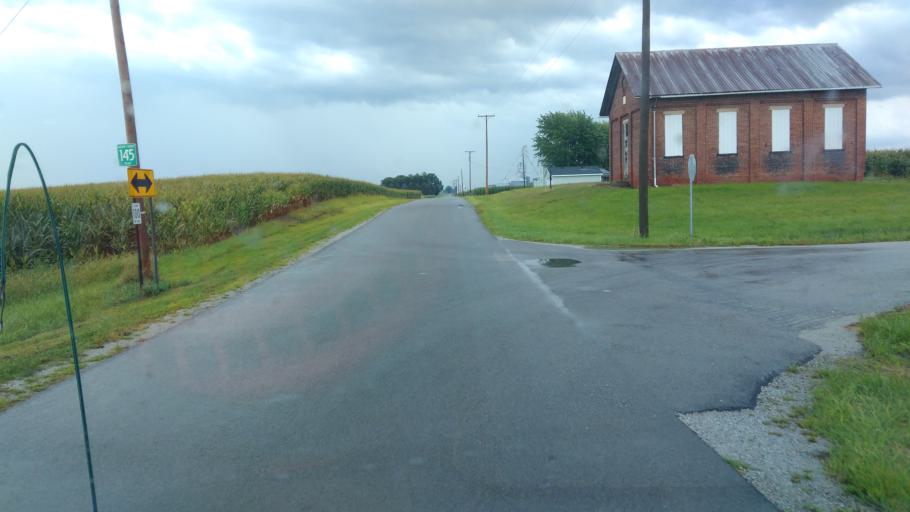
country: US
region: Ohio
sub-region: Hardin County
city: Kenton
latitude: 40.6894
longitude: -83.6340
